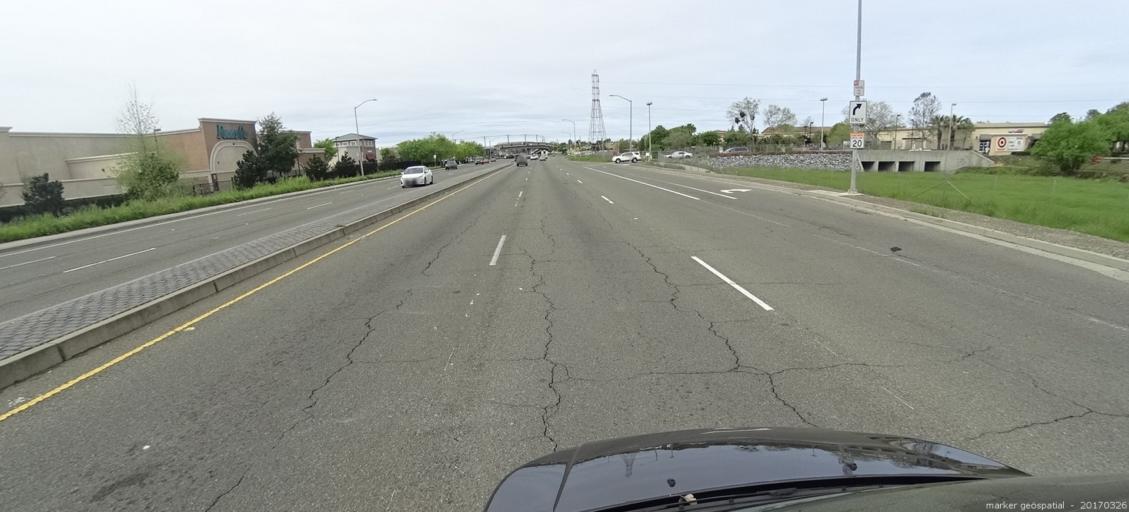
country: US
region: California
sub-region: Sacramento County
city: Laguna
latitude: 38.4573
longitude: -121.4143
